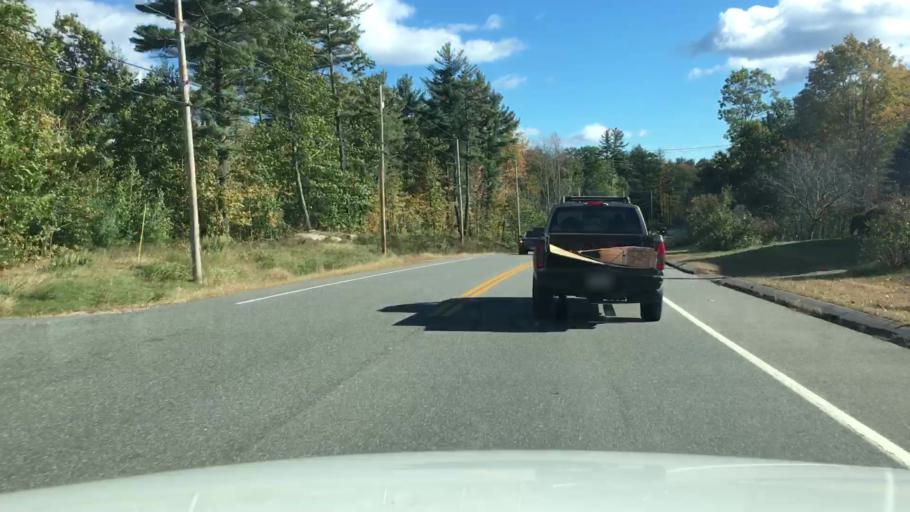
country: US
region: Maine
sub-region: York County
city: Wells Beach Station
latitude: 43.3526
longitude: -70.6493
